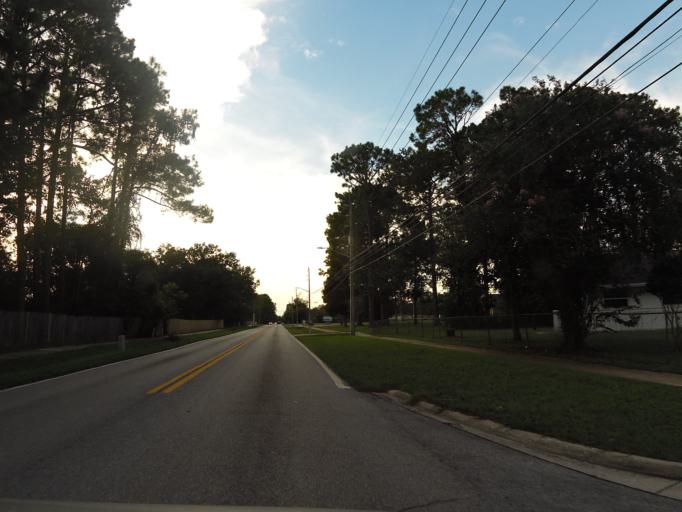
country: US
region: Florida
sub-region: Clay County
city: Bellair-Meadowbrook Terrace
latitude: 30.2755
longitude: -81.7814
